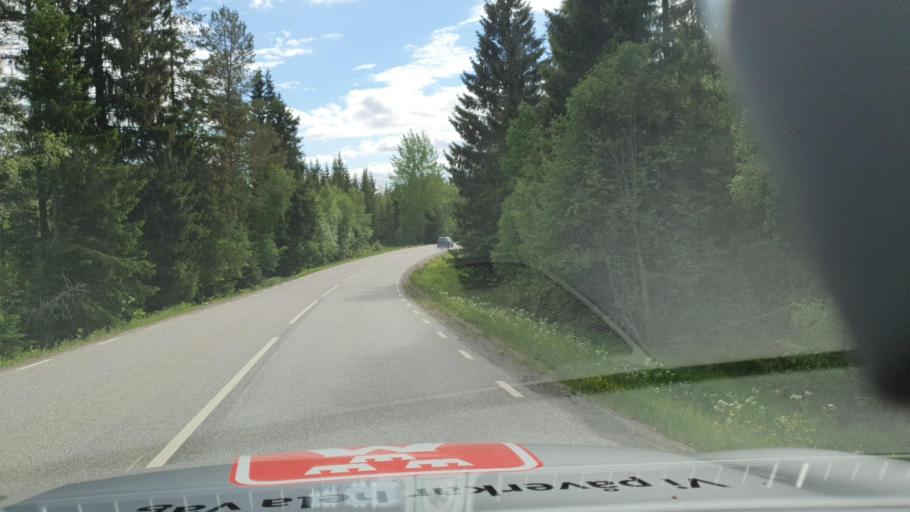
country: SE
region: Vaesternorrland
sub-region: Kramfors Kommun
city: Nordingra
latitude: 62.9091
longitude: 18.1601
